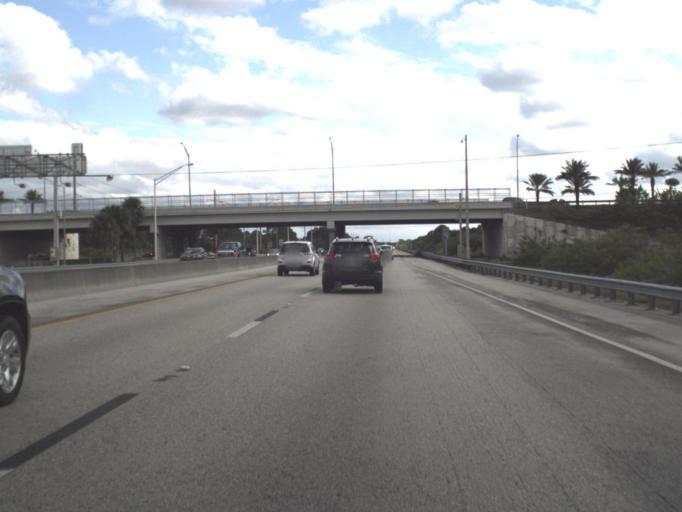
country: US
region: Florida
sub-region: Saint Lucie County
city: Port Saint Lucie
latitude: 27.2744
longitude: -80.3591
